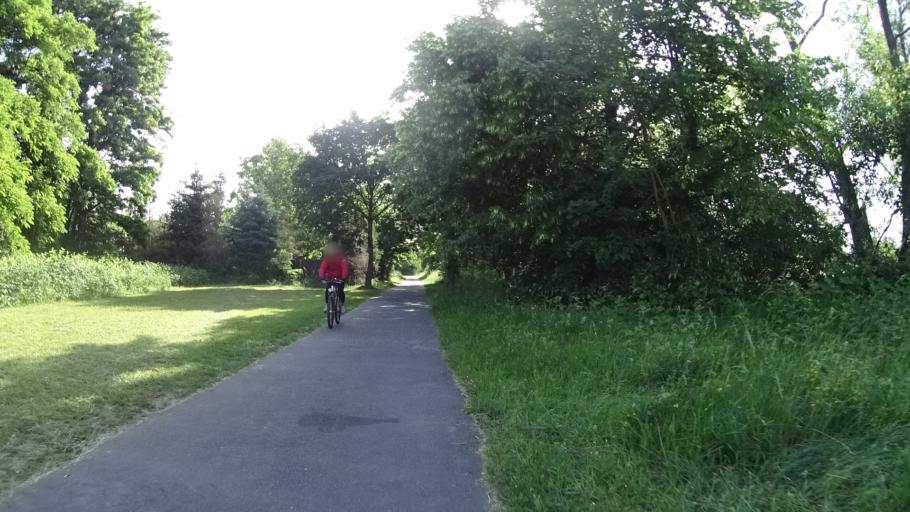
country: DE
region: Bavaria
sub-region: Regierungsbezirk Unterfranken
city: Kahl am Main
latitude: 50.0459
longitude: 9.0033
